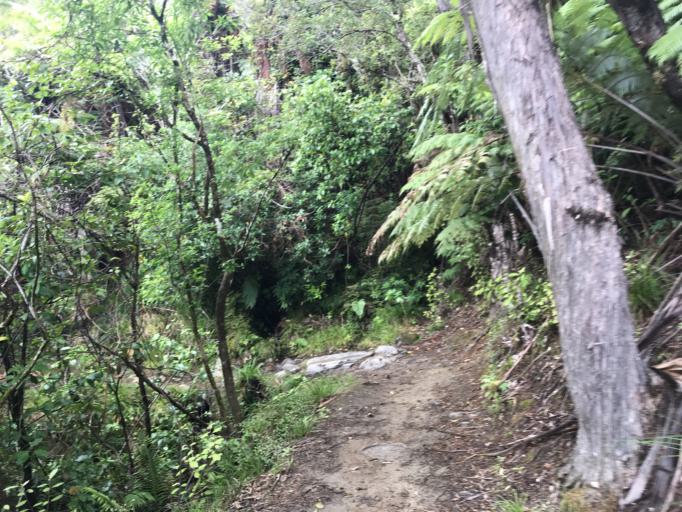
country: NZ
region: Marlborough
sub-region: Marlborough District
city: Picton
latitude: -41.2287
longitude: 173.9583
